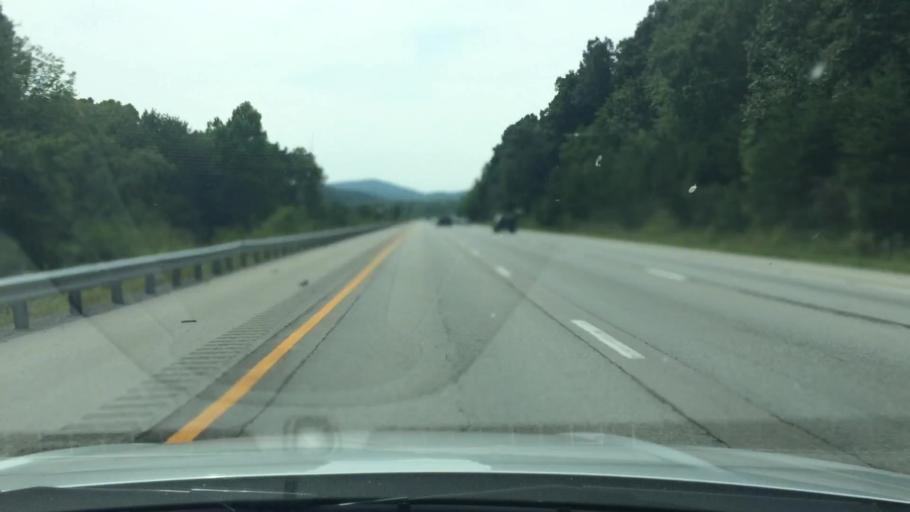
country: US
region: Kentucky
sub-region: Madison County
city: Berea
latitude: 37.5282
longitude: -84.3205
